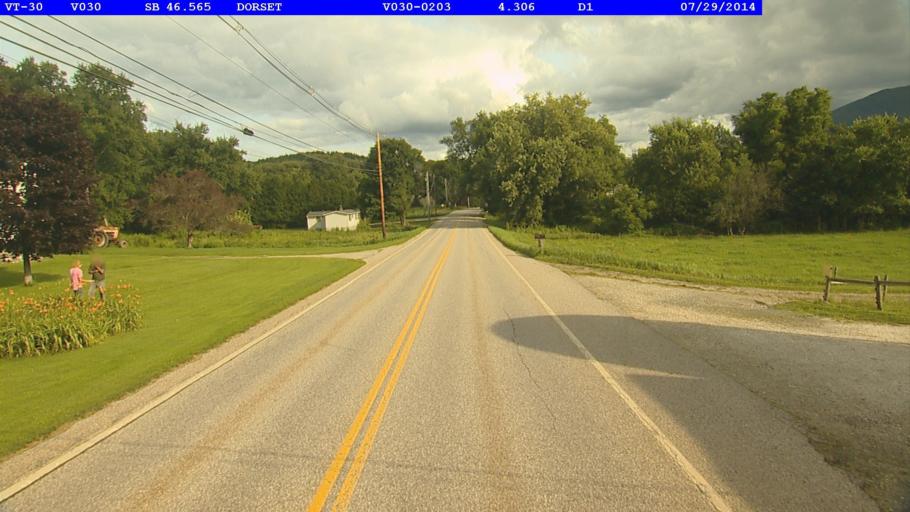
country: US
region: Vermont
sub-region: Bennington County
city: Manchester Center
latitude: 43.2666
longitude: -73.1073
